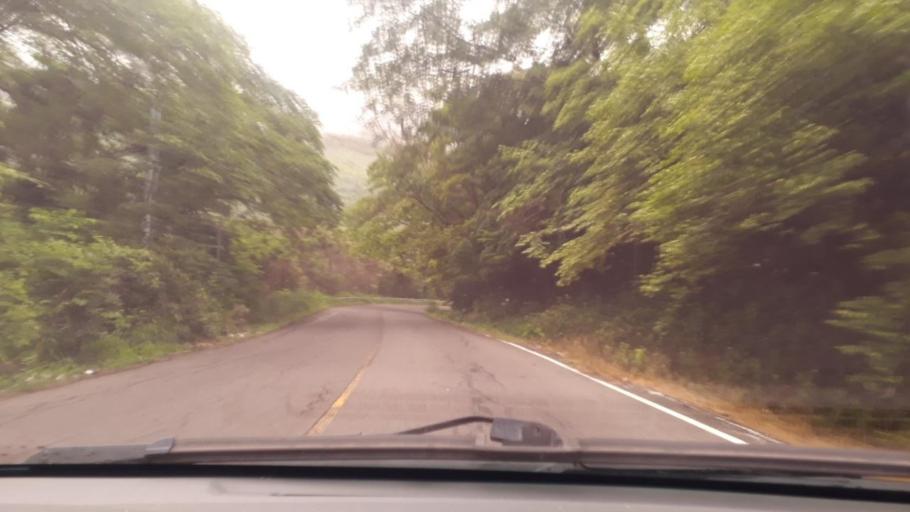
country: GT
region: Jutiapa
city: Comapa
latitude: 14.0926
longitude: -89.9629
